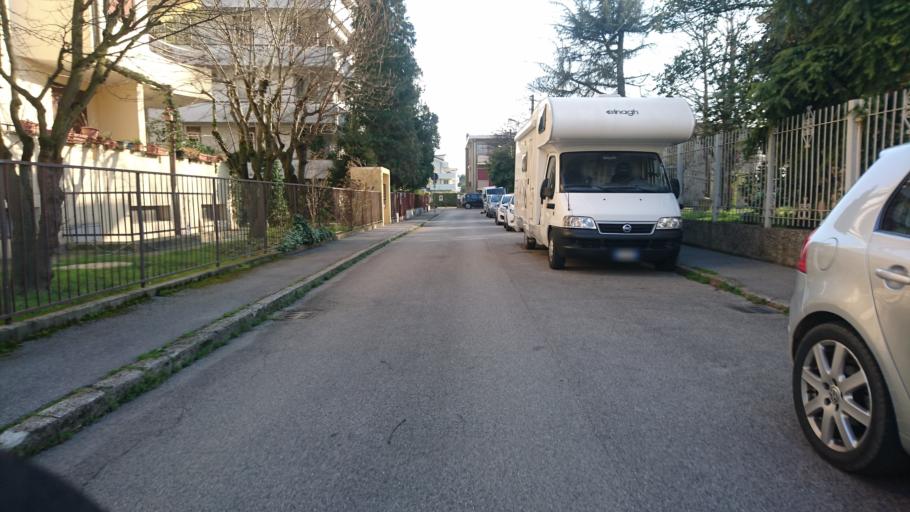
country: IT
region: Veneto
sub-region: Provincia di Padova
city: Mandriola-Sant'Agostino
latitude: 45.3886
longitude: 11.8566
